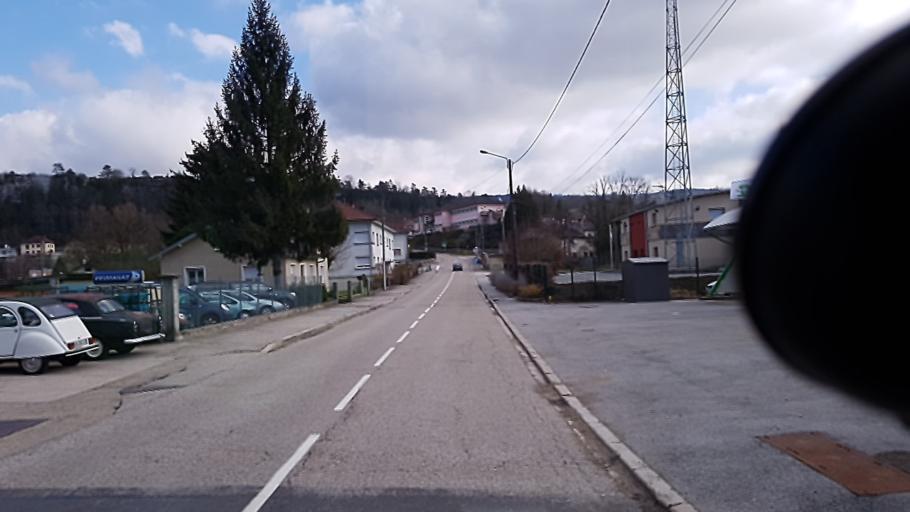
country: FR
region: Rhone-Alpes
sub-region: Departement de l'Ain
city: Dortan
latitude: 46.3216
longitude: 5.6562
